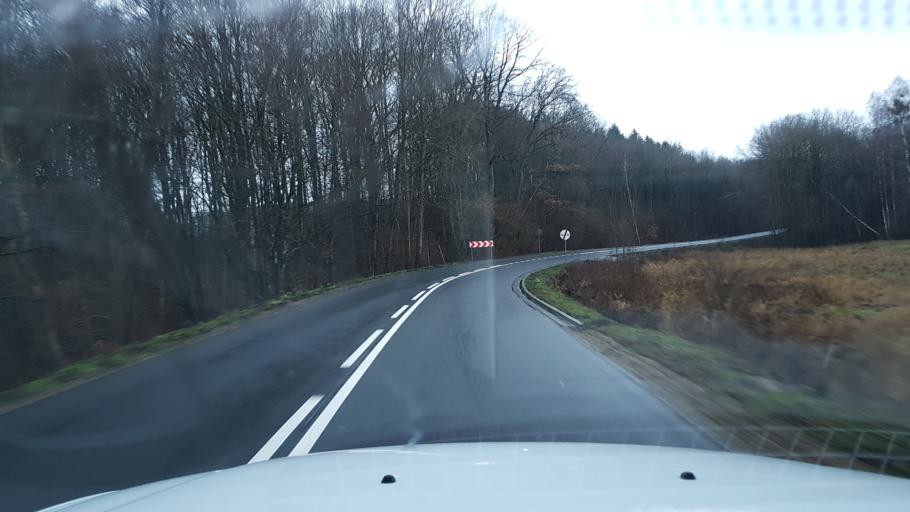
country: PL
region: West Pomeranian Voivodeship
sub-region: Powiat kolobrzeski
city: Ryman
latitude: 53.9534
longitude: 15.4949
